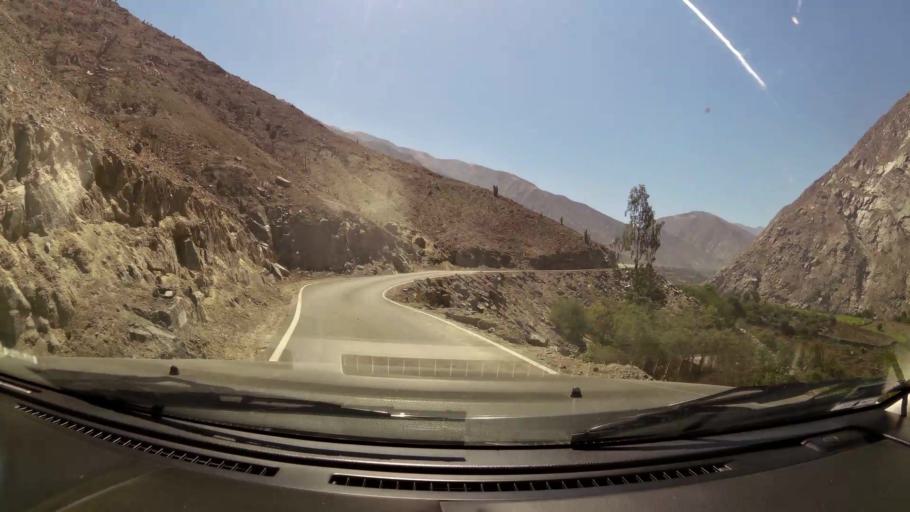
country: PE
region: Ica
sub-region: Provincia de Pisco
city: Huancano
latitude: -13.8294
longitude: -75.5408
